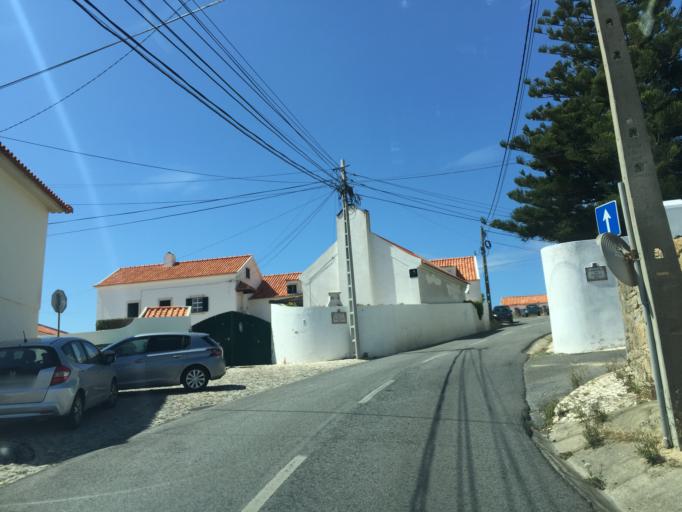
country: PT
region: Lisbon
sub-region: Sintra
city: Colares
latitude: 38.8411
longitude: -9.4610
